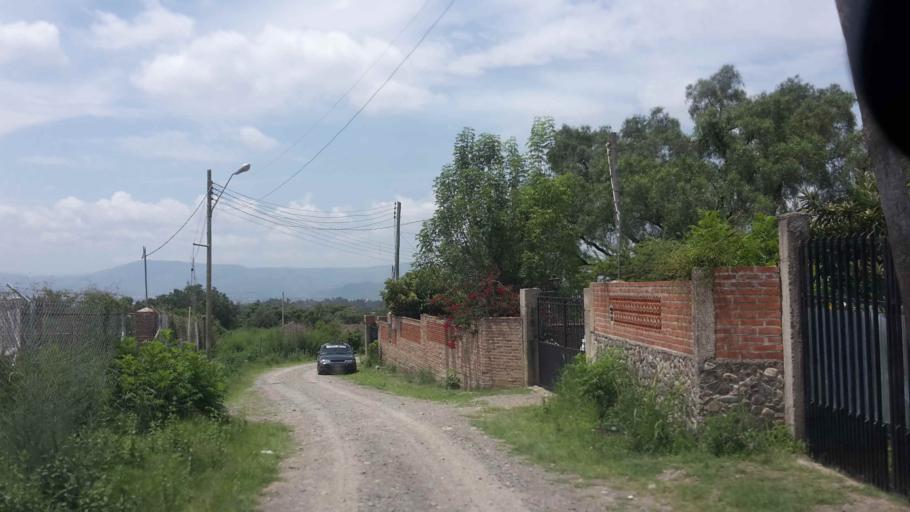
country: BO
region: Cochabamba
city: Cochabamba
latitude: -17.3307
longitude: -66.2137
